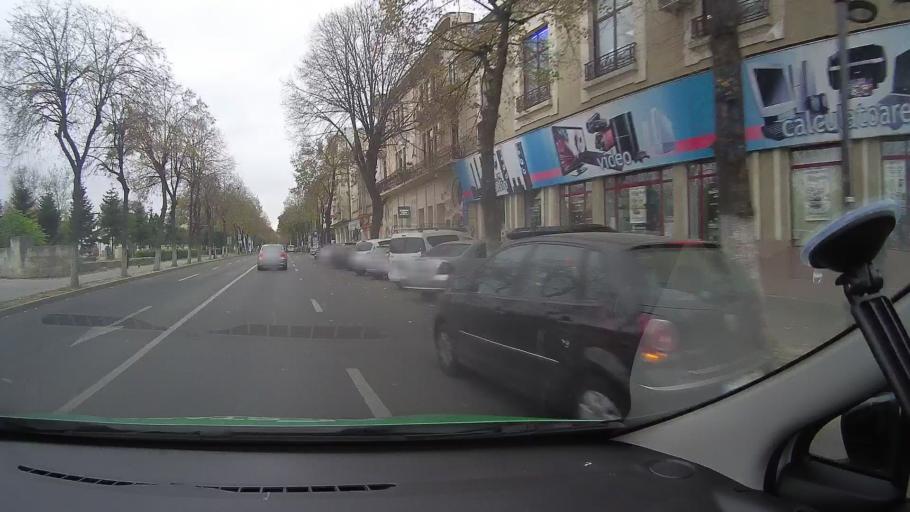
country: RO
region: Constanta
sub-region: Municipiul Constanta
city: Constanta
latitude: 44.1782
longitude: 28.6511
